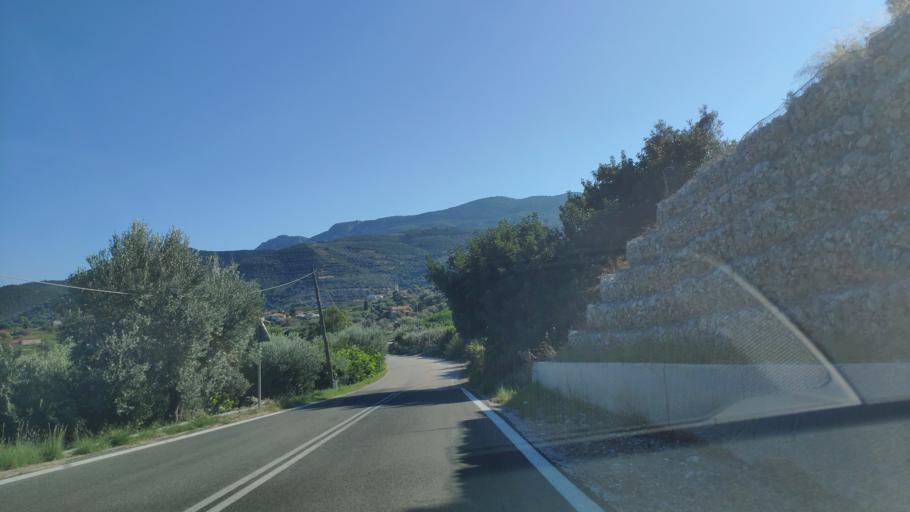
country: GR
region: Peloponnese
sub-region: Nomos Argolidos
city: Didyma
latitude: 37.5467
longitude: 23.2840
